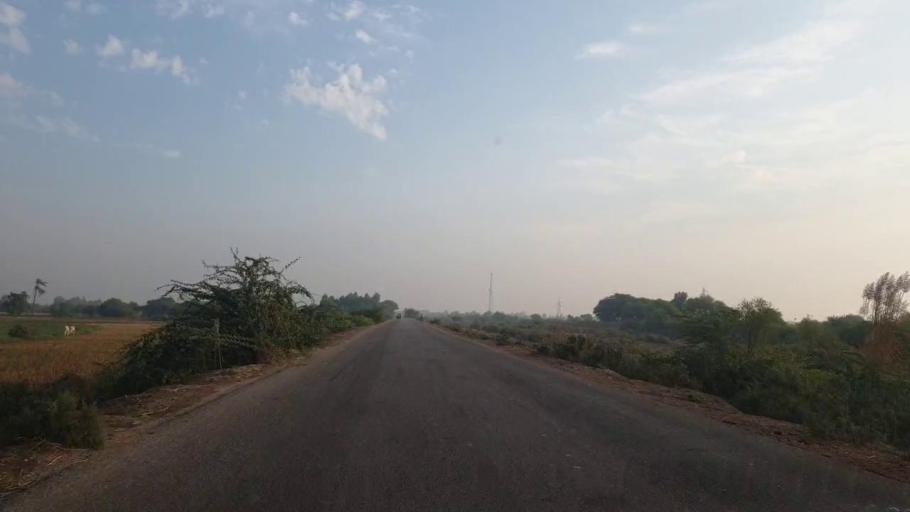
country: PK
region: Sindh
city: Tando Bago
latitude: 24.7022
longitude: 68.9251
